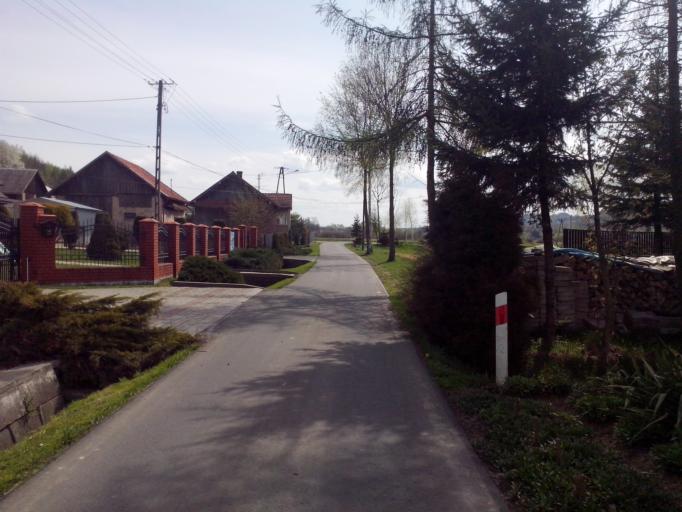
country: PL
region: Subcarpathian Voivodeship
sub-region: Powiat strzyzowski
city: Jawornik
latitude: 49.8092
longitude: 21.8721
